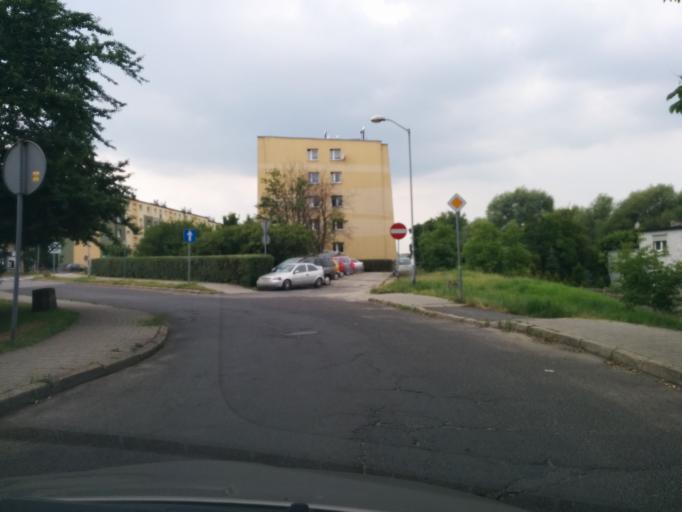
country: PL
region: Silesian Voivodeship
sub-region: Ruda Slaska
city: Ruda Slaska
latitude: 50.2412
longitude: 18.8340
